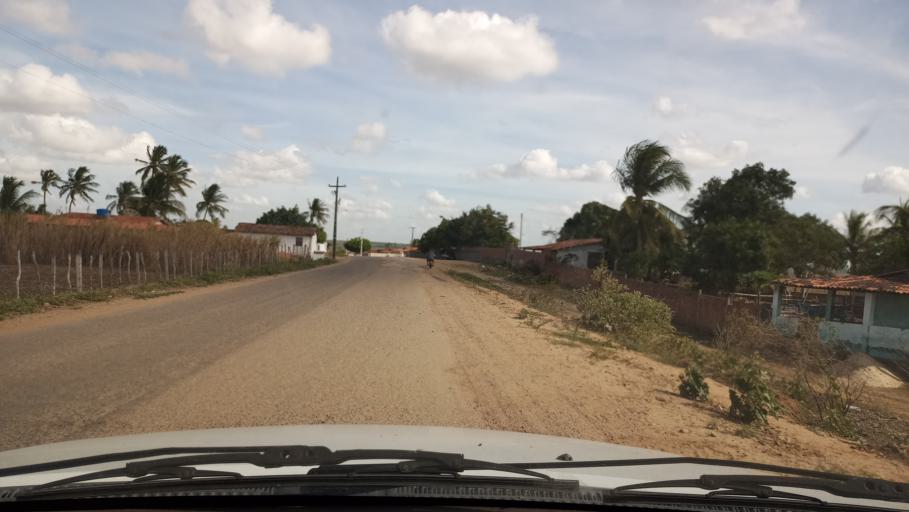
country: BR
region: Rio Grande do Norte
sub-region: Goianinha
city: Goianinha
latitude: -6.3211
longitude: -35.3080
